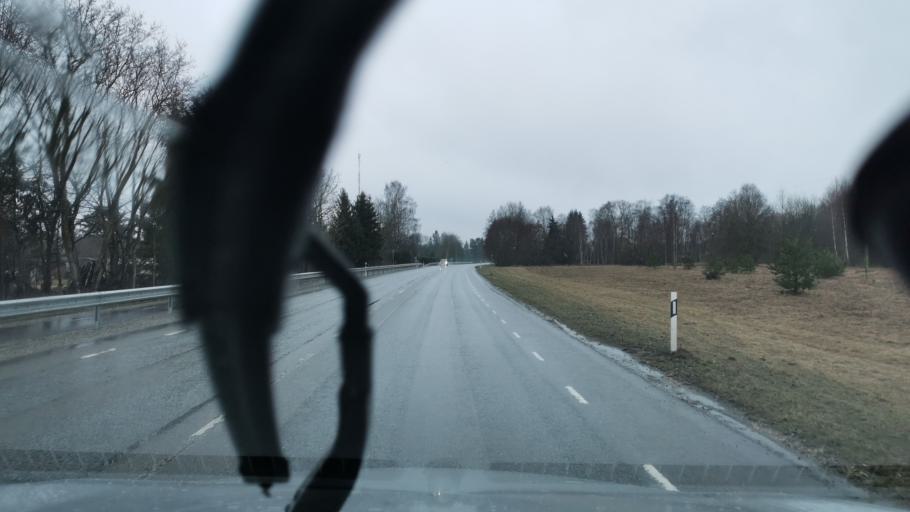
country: EE
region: Harju
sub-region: Kiili vald
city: Kiili
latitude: 59.3306
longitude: 24.7730
